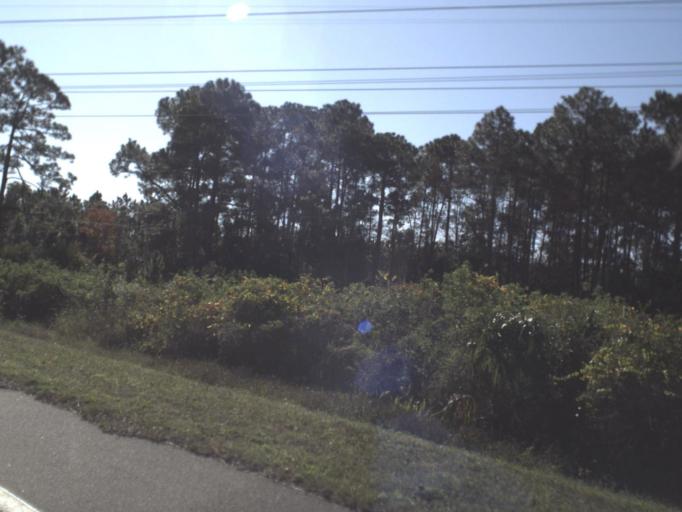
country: US
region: Florida
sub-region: Volusia County
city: Holly Hill
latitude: 29.2158
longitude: -81.0796
